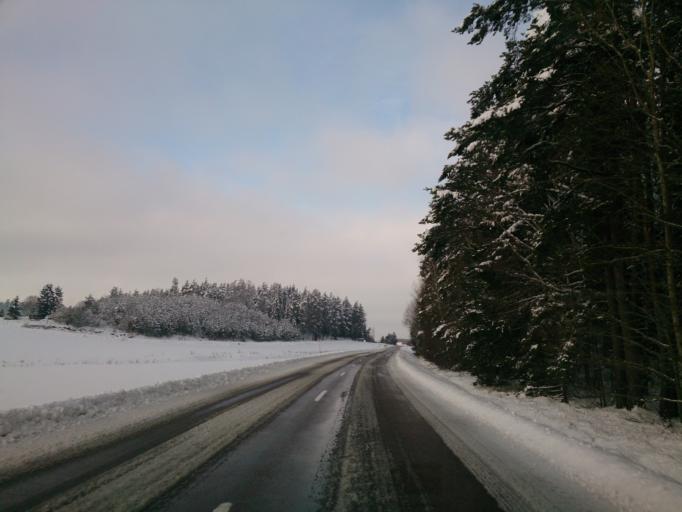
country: SE
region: OEstergoetland
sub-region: Linkopings Kommun
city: Linghem
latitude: 58.4361
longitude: 15.8939
